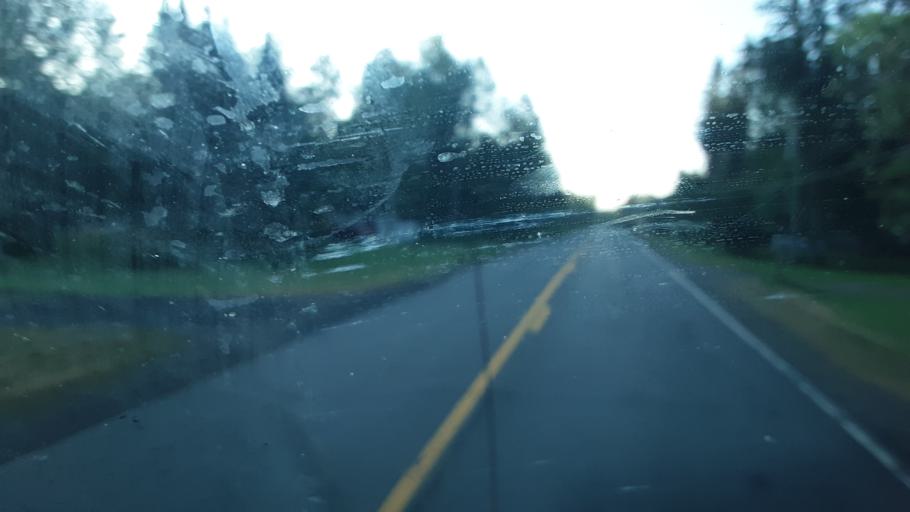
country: US
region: Maine
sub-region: Aroostook County
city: Presque Isle
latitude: 46.7551
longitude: -68.0607
